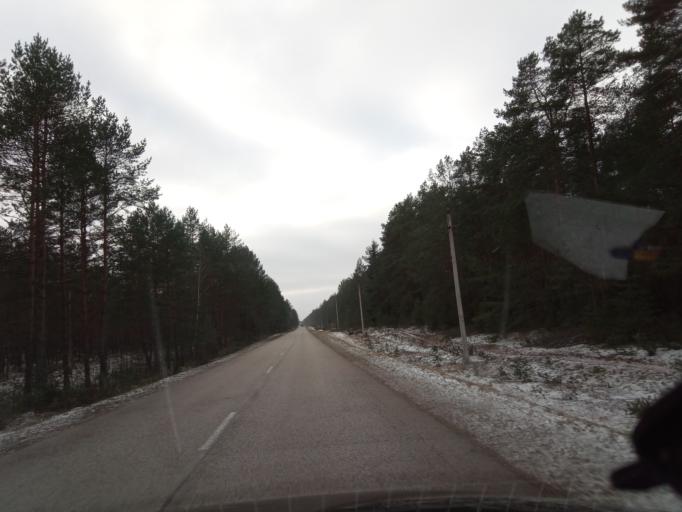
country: LT
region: Alytaus apskritis
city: Varena
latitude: 54.0382
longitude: 24.3725
